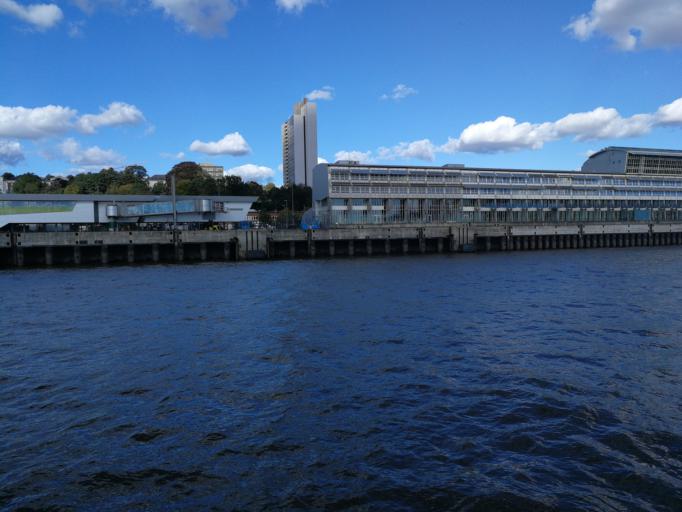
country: DE
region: Hamburg
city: Altona
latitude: 53.5420
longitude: 9.9388
